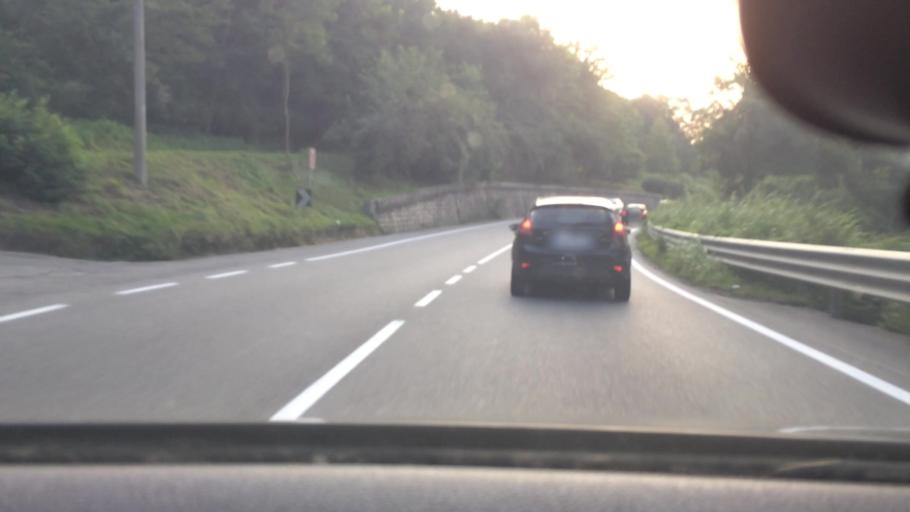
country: IT
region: Lombardy
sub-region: Provincia di Lecco
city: Perego
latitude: 45.7429
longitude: 9.3505
